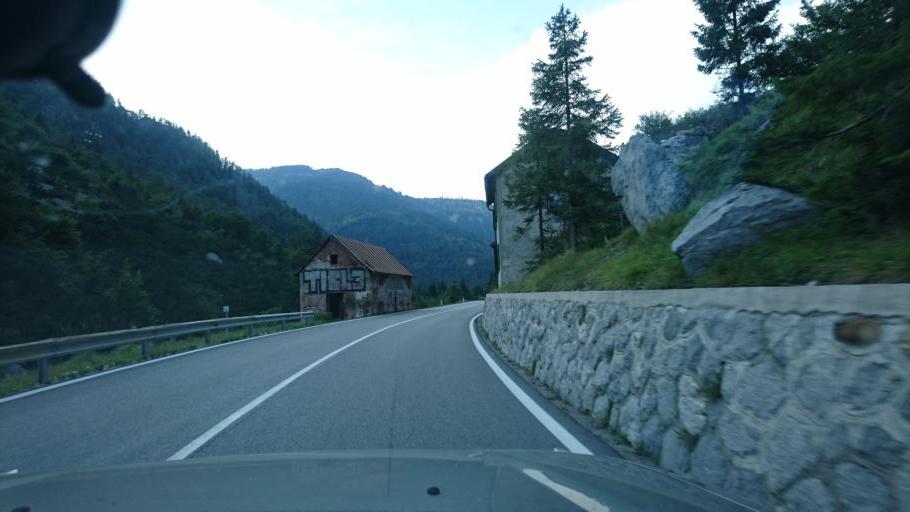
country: IT
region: Friuli Venezia Giulia
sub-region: Provincia di Udine
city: Tarvisio
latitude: 46.4614
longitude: 13.5737
